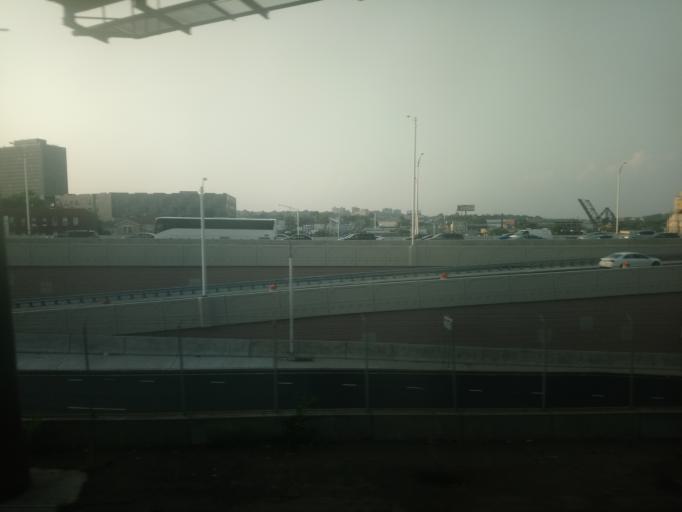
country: US
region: New Jersey
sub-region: Hudson County
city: East Newark
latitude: 40.7475
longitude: -74.1683
